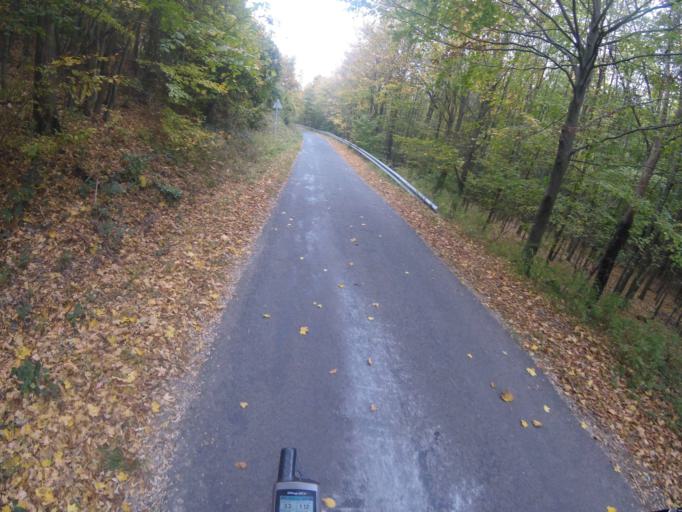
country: HU
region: Gyor-Moson-Sopron
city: Bakonyszentlaszlo
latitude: 47.2893
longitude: 17.7589
